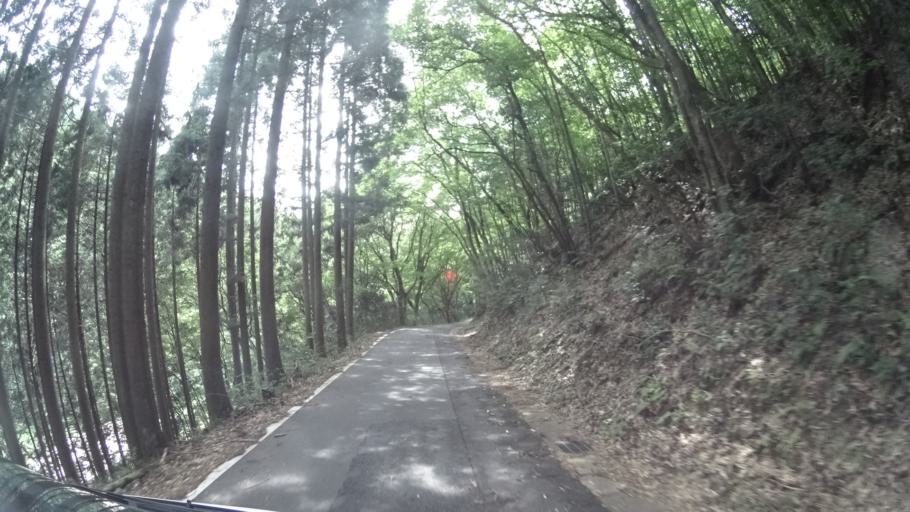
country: JP
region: Kyoto
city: Fukuchiyama
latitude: 35.3673
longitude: 135.1721
